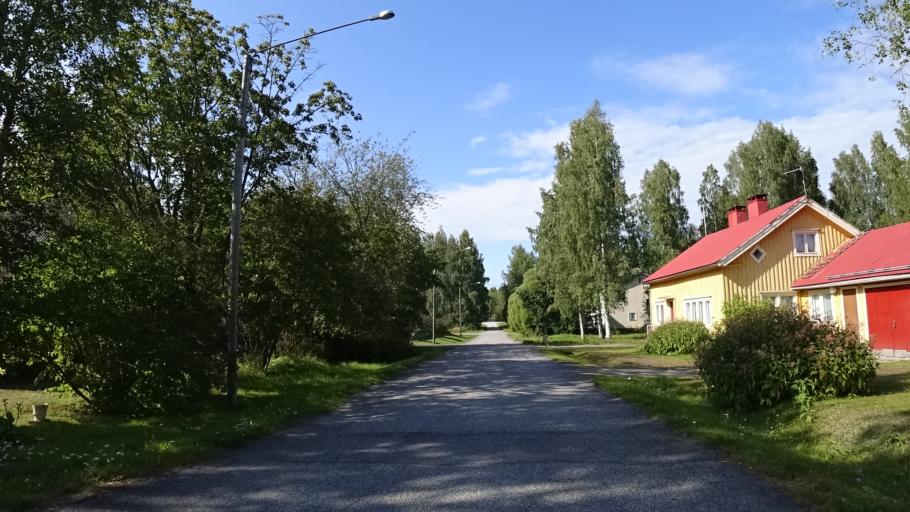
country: FI
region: North Karelia
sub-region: Joensuu
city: Eno
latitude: 62.7995
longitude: 30.1500
